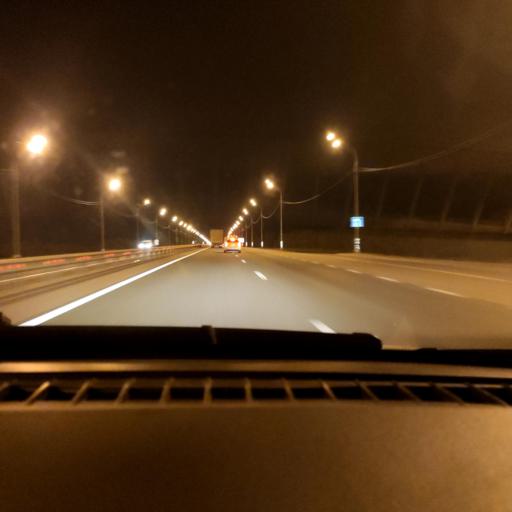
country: RU
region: Lipetsk
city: Khlevnoye
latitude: 52.2320
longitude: 39.0882
